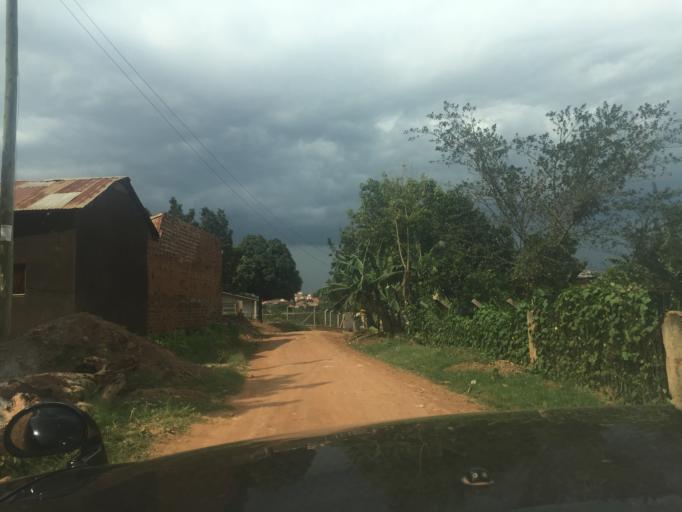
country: UG
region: Central Region
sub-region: Wakiso District
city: Kireka
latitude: 0.4063
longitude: 32.6264
